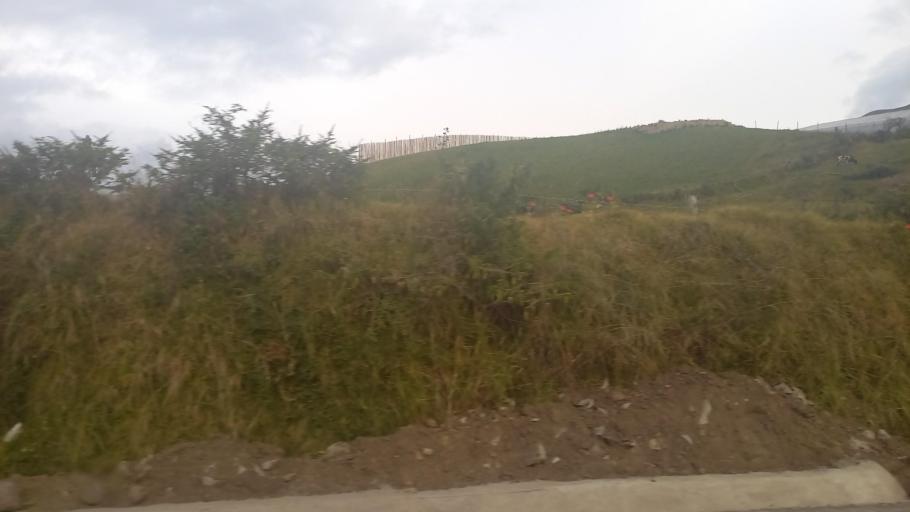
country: EC
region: Pichincha
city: Cayambe
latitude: 0.1297
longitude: -78.0688
